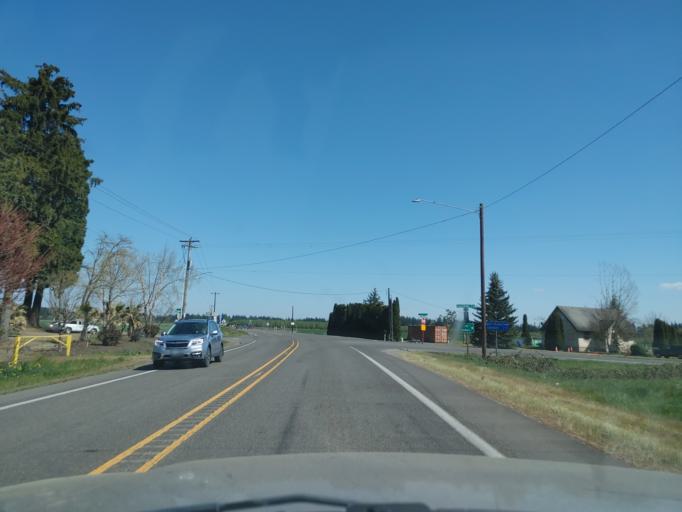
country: US
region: Oregon
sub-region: Yamhill County
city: Newberg
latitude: 45.2343
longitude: -122.9112
